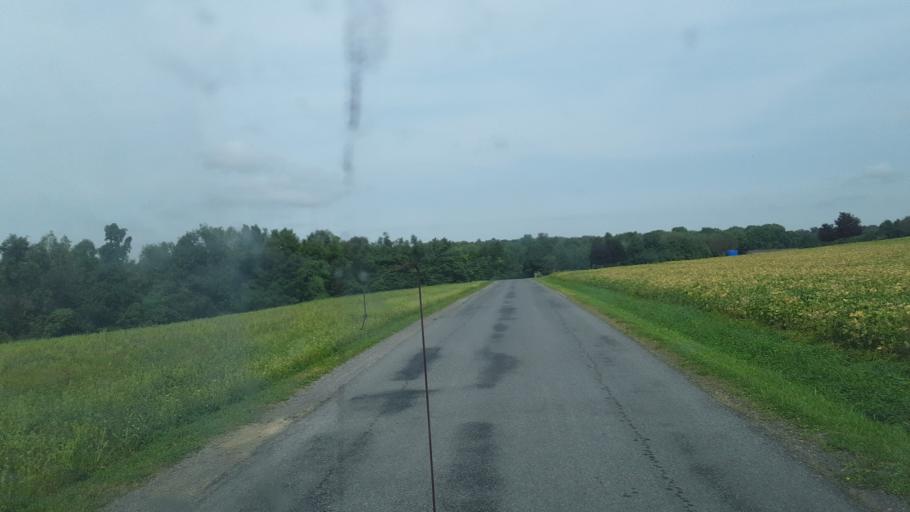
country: US
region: Pennsylvania
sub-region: Jefferson County
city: Punxsutawney
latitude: 40.9448
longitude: -79.0689
